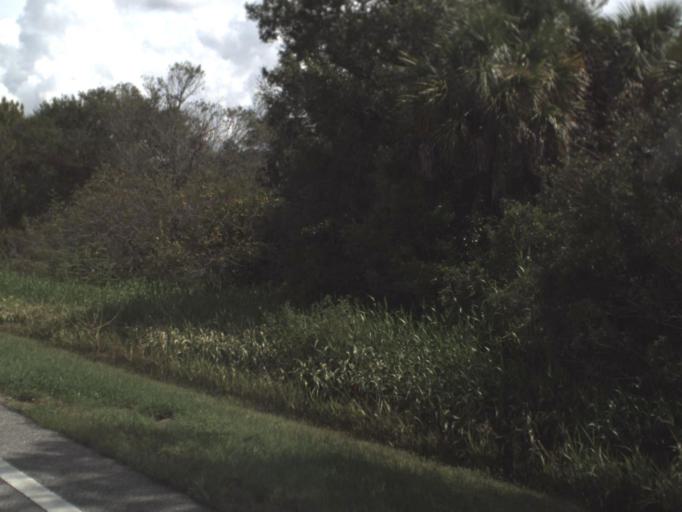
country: US
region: Florida
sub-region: Sarasota County
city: Warm Mineral Springs
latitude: 27.2190
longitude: -82.2816
